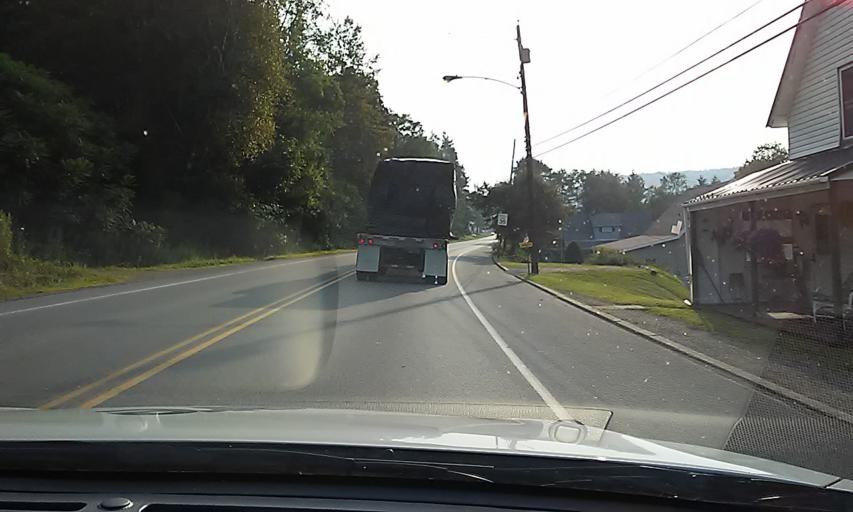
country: US
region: Pennsylvania
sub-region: McKean County
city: Smethport
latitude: 41.7063
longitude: -78.5762
